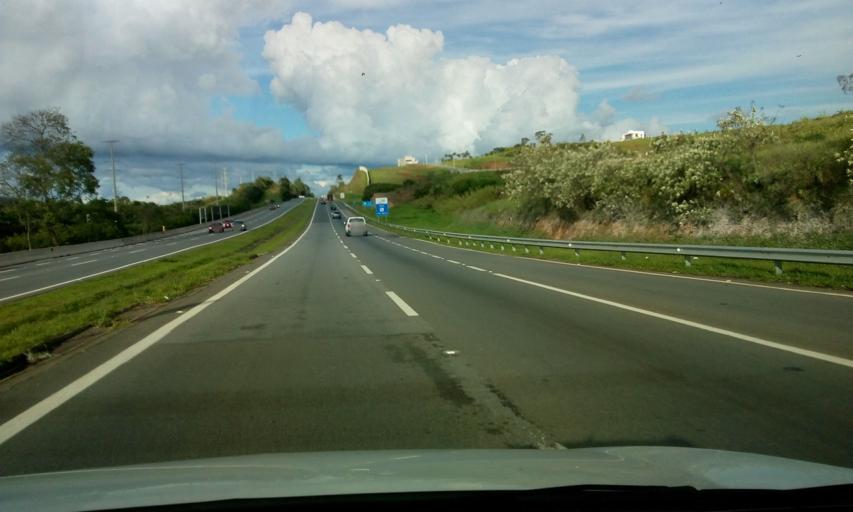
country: BR
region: Sao Paulo
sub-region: Jundiai
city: Jundiai
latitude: -23.1599
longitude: -46.8997
